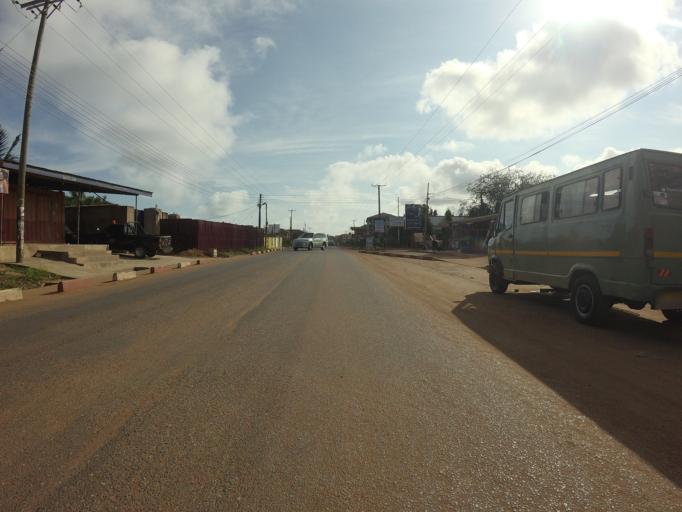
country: GH
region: Greater Accra
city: Teshi Old Town
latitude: 5.5752
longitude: -0.1391
